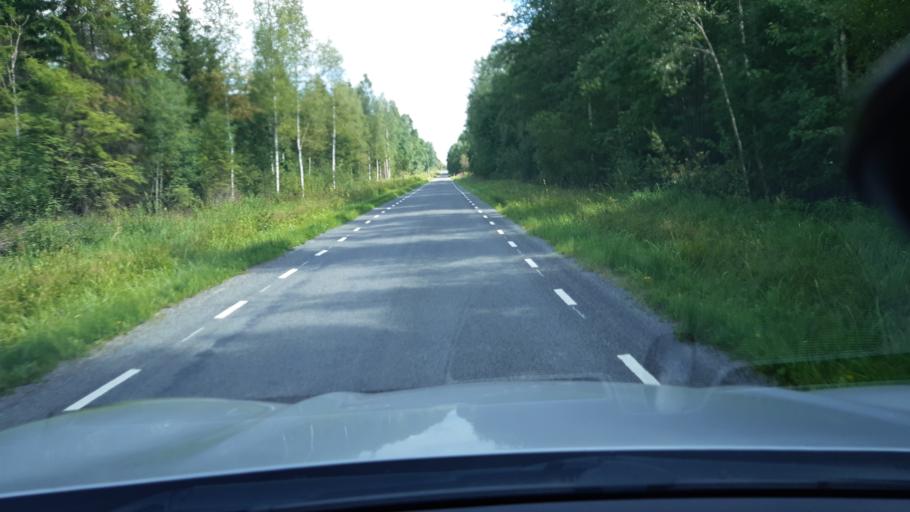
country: EE
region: Raplamaa
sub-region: Jaervakandi vald
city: Jarvakandi
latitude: 58.7515
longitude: 24.9259
